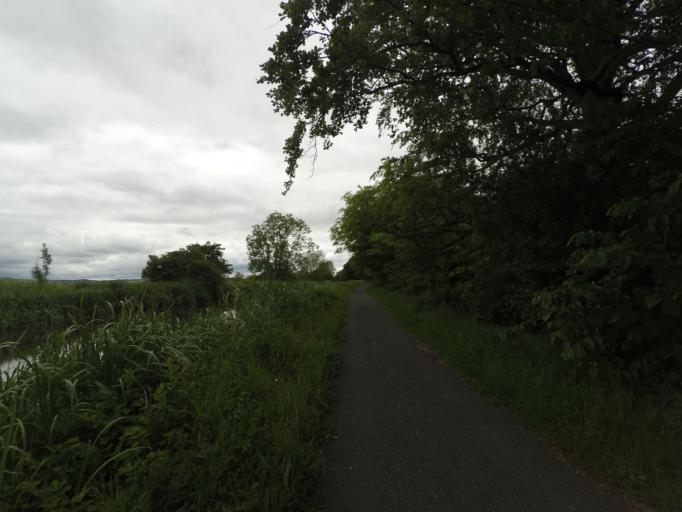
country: GB
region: Scotland
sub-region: West Lothian
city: Broxburn
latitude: 55.9751
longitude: -3.5206
